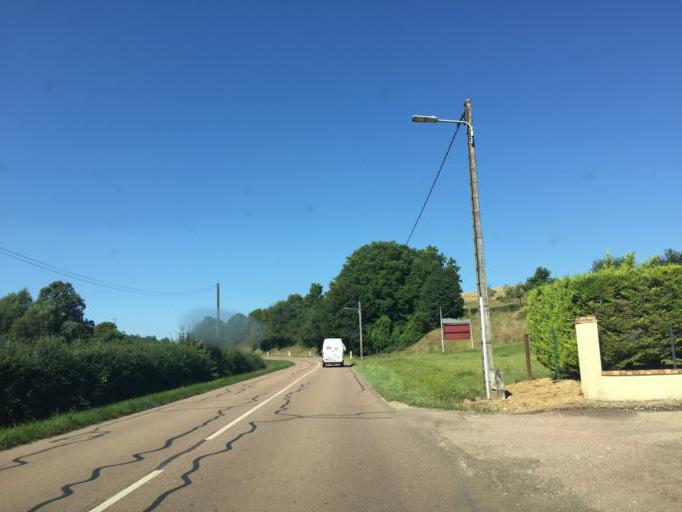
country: FR
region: Bourgogne
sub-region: Departement de la Nievre
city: Clamecy
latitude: 47.4496
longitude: 3.4966
